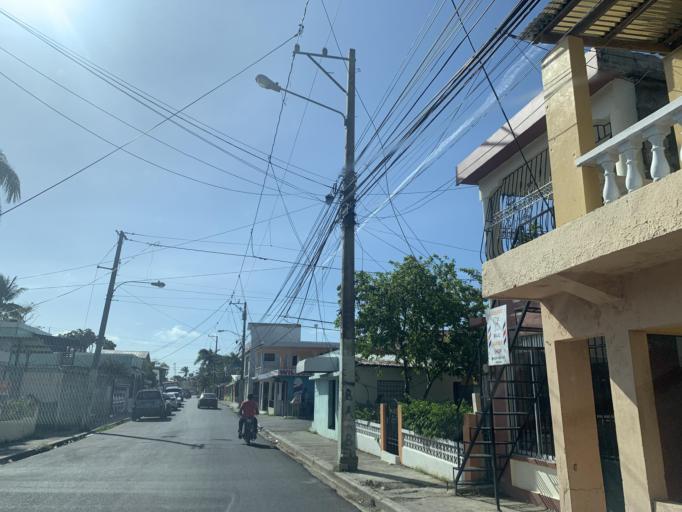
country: DO
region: Puerto Plata
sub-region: Puerto Plata
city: Puerto Plata
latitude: 19.7946
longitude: -70.6963
